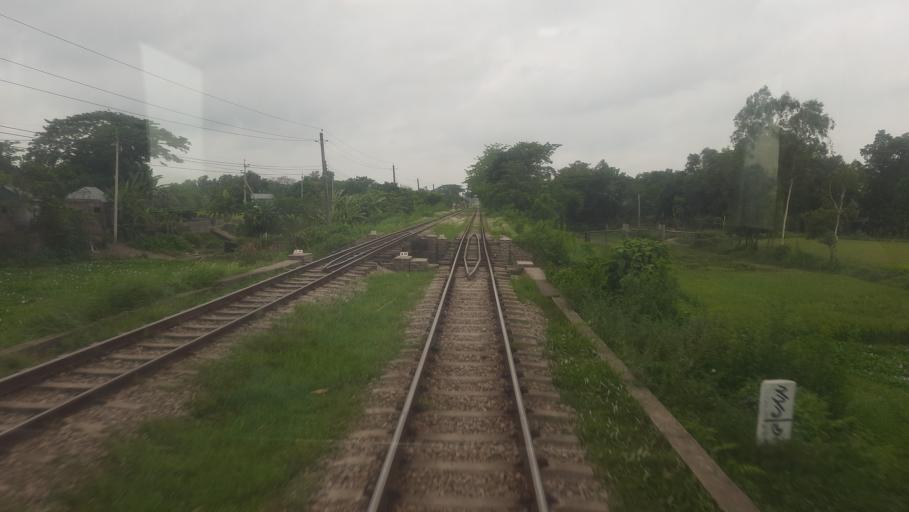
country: BD
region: Dhaka
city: Bhairab Bazar
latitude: 23.9834
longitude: 91.0736
